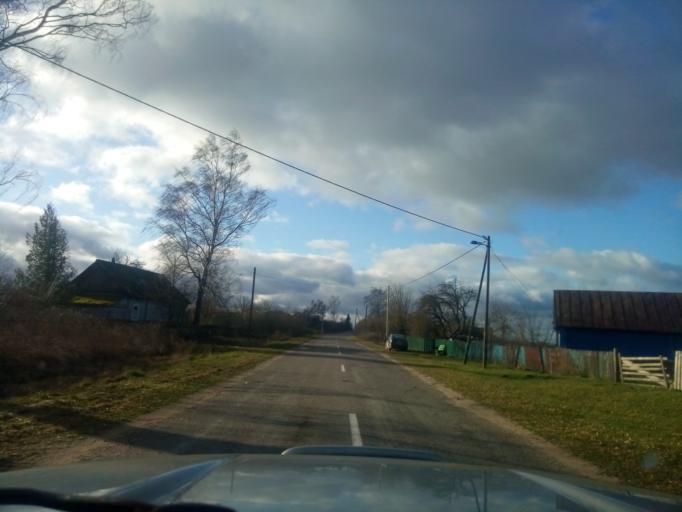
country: BY
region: Minsk
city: Tsimkavichy
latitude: 53.1983
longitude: 26.9318
